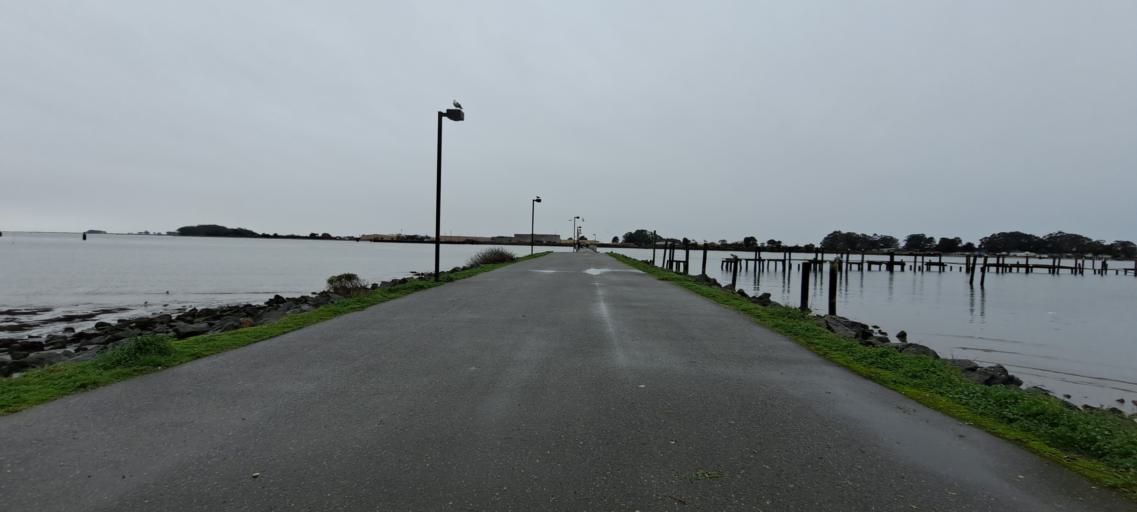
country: US
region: California
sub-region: Humboldt County
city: Bayview
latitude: 40.7907
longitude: -124.1871
